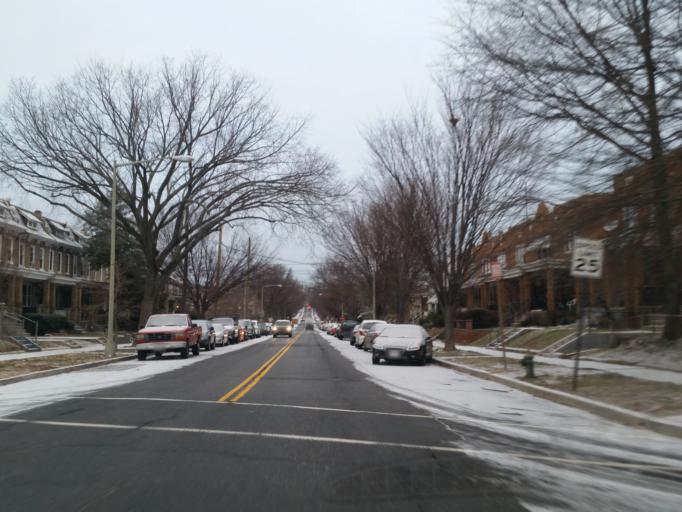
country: US
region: Maryland
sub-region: Montgomery County
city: Takoma Park
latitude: 38.9509
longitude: -77.0241
